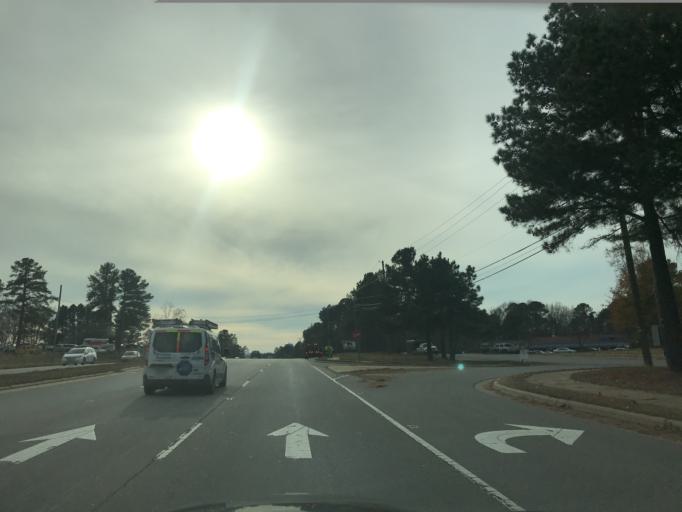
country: US
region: North Carolina
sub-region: Wake County
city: Knightdale
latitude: 35.8552
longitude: -78.5560
